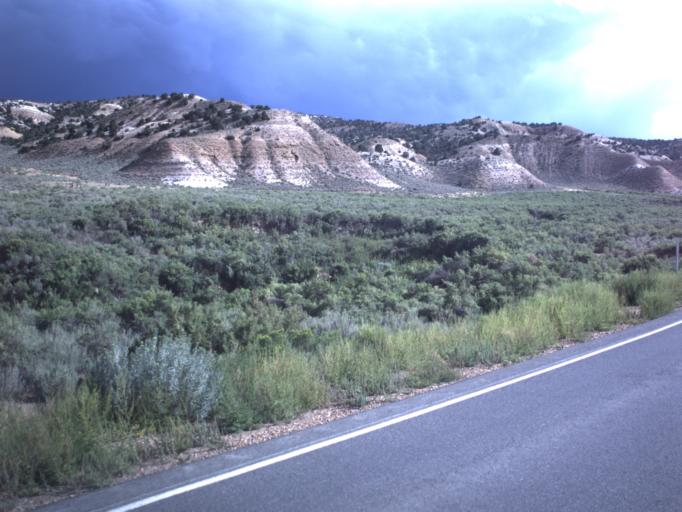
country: US
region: Utah
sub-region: Duchesne County
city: Duchesne
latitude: 40.1353
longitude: -110.4278
